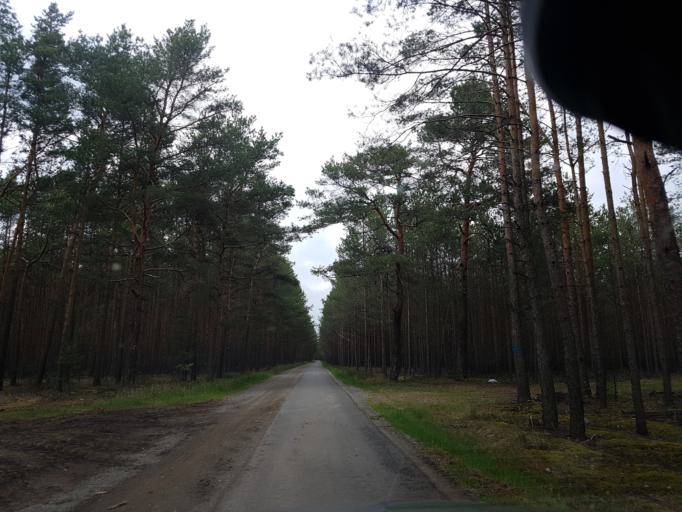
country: DE
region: Brandenburg
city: Crinitz
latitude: 51.6806
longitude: 13.7796
